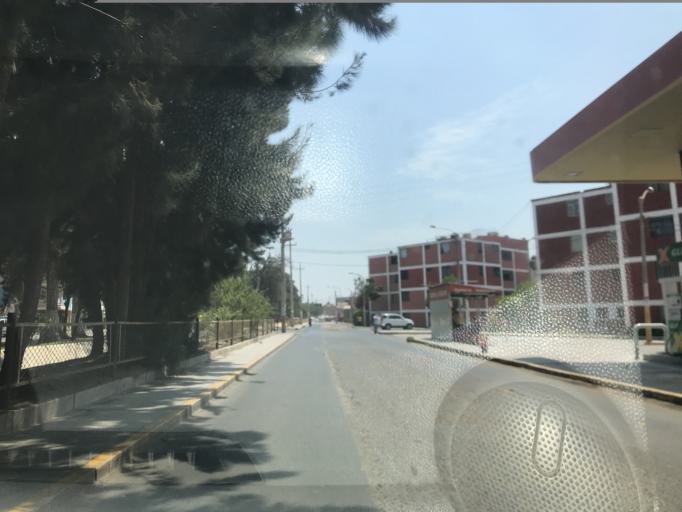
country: PE
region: Lambayeque
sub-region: Provincia de Chiclayo
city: Chiclayo
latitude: -6.7786
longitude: -79.8387
